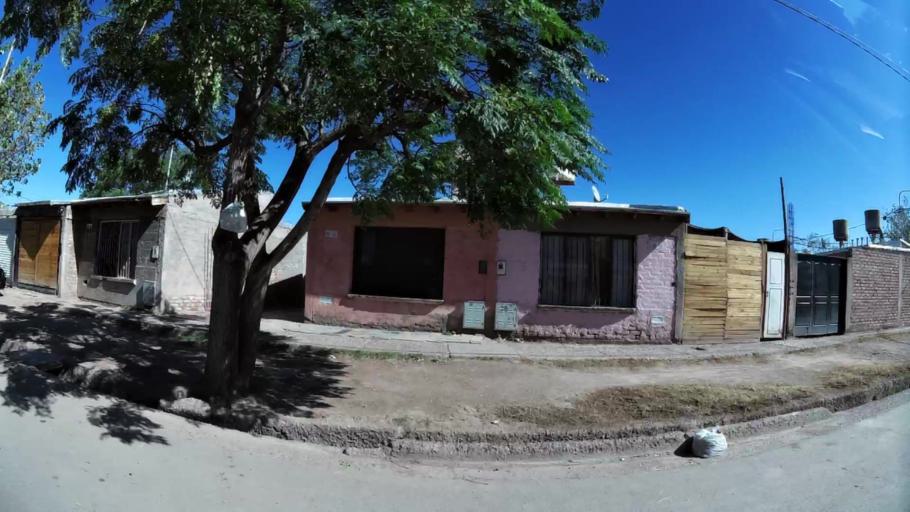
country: AR
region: Mendoza
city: Las Heras
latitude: -32.8388
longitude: -68.8125
